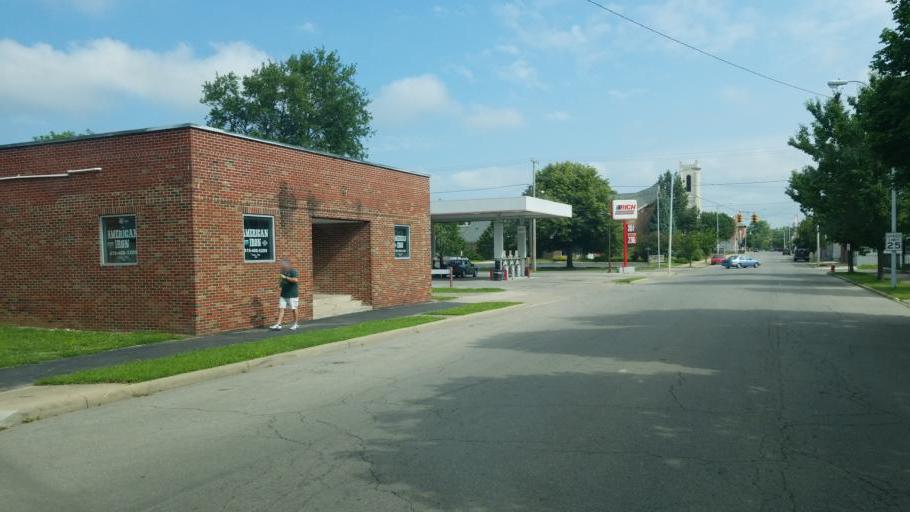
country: US
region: Ohio
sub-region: Crawford County
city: Galion
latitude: 40.7304
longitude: -82.7896
